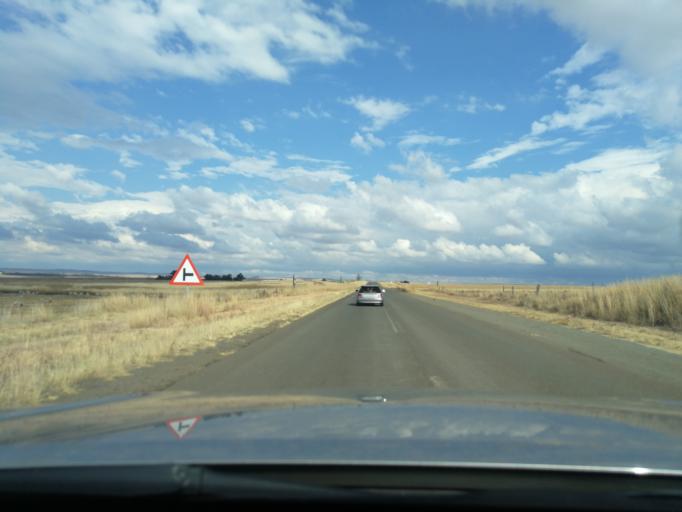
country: ZA
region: Orange Free State
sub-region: Fezile Dabi District Municipality
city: Frankfort
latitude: -27.4375
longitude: 28.5125
